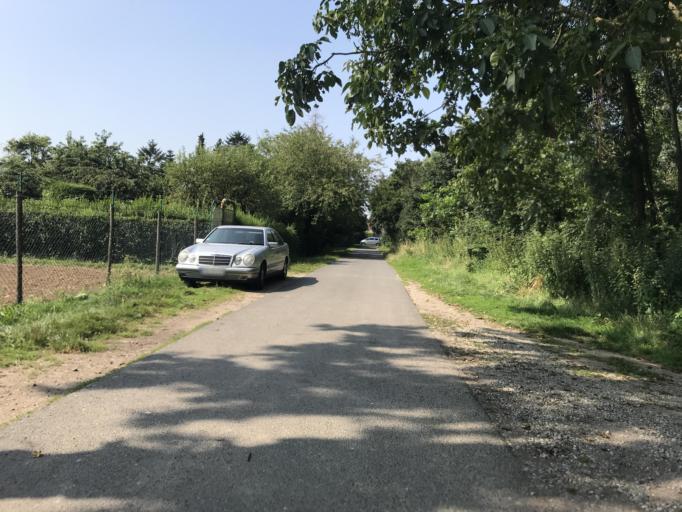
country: DE
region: Hesse
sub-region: Regierungsbezirk Darmstadt
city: Hochheim am Main
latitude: 50.0168
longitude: 8.3601
